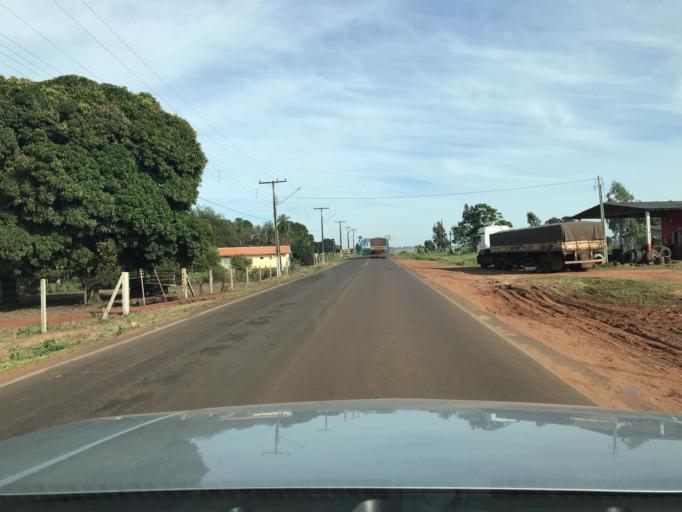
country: BR
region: Mato Grosso do Sul
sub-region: Iguatemi
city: Iguatemi
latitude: -23.6627
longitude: -54.5674
